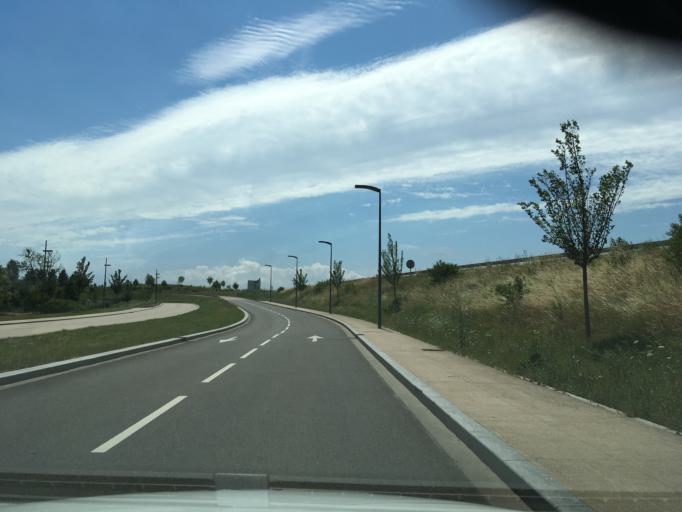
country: FR
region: Lorraine
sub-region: Departement de la Moselle
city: Peltre
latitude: 49.0867
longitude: 6.2318
